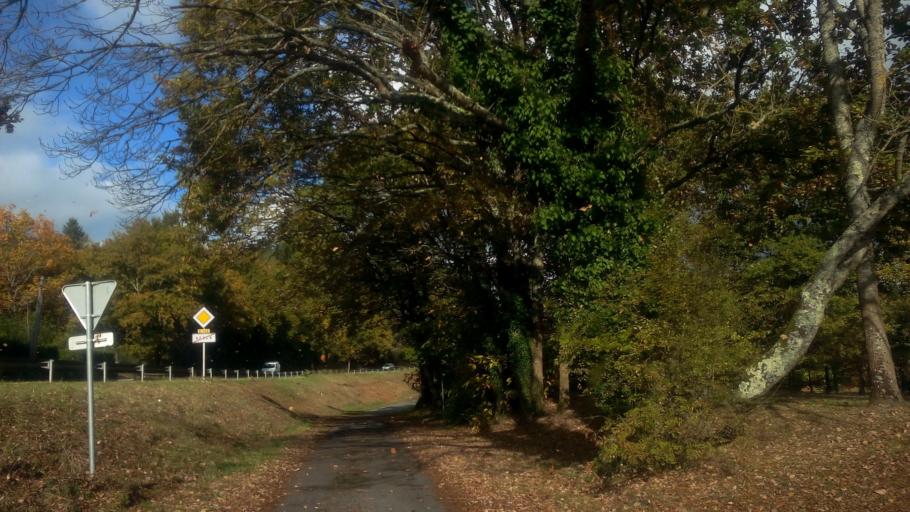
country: FR
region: Brittany
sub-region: Departement d'Ille-et-Vilaine
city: Redon
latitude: 47.6614
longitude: -2.0844
